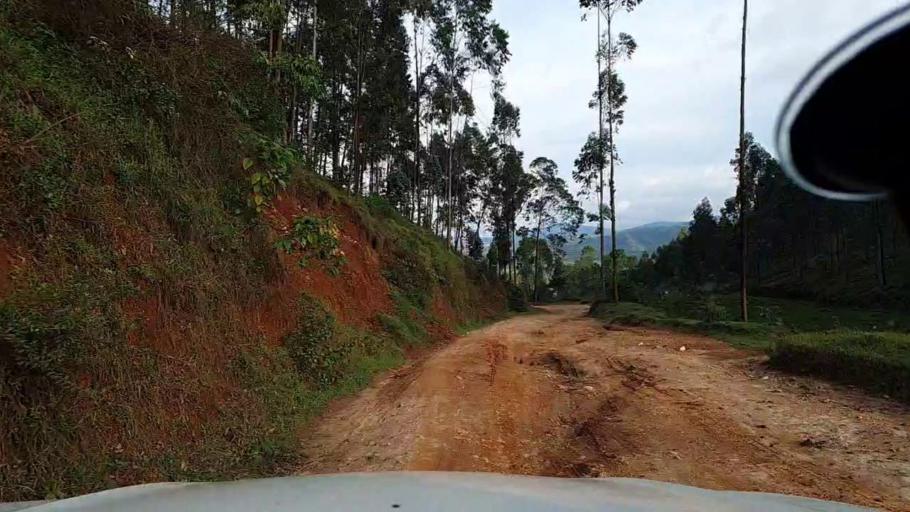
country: RW
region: Southern Province
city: Gitarama
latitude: -2.1872
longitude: 29.5726
